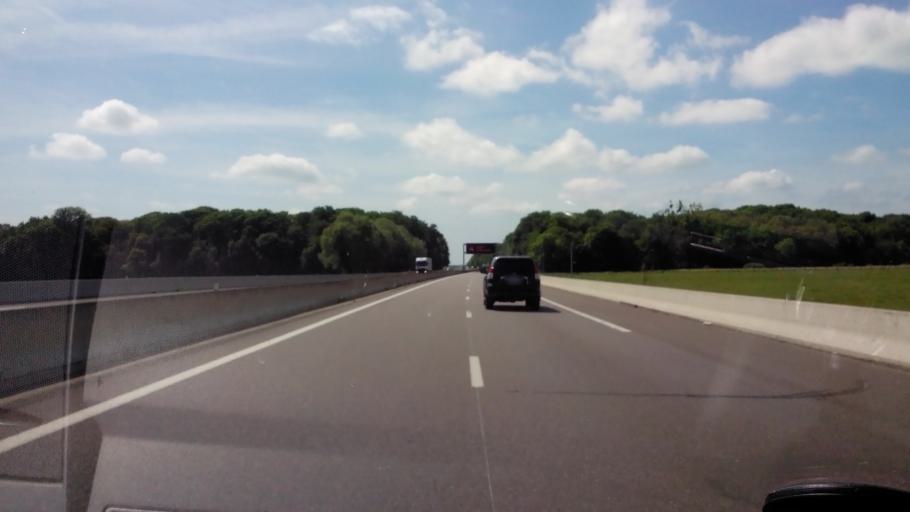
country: FR
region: Lorraine
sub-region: Departement des Vosges
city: Chatenois
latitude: 48.3253
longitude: 5.8563
